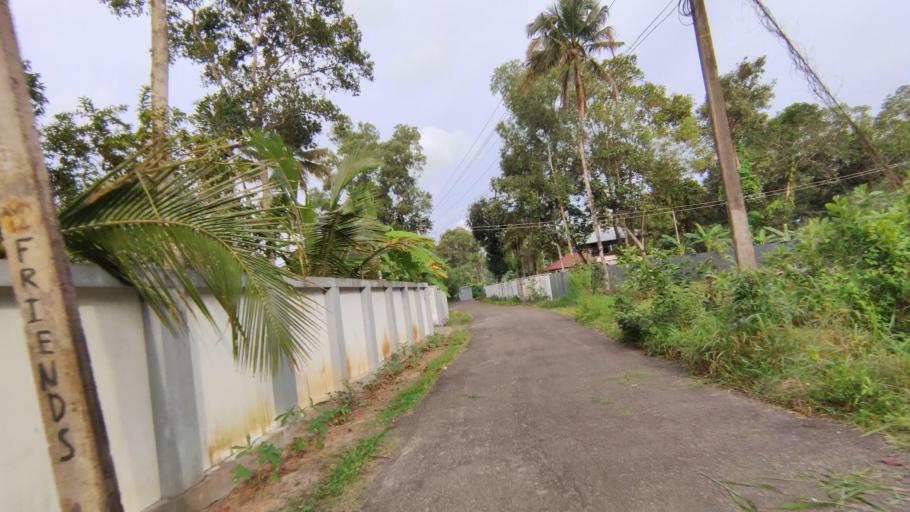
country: IN
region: Kerala
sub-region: Alappuzha
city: Shertallai
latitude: 9.6186
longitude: 76.3456
